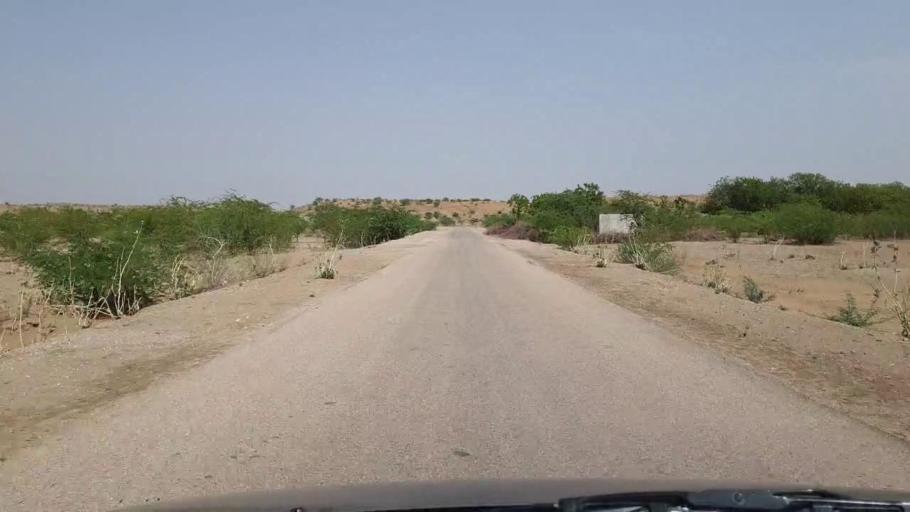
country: PK
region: Sindh
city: Chor
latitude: 25.4732
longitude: 70.5138
